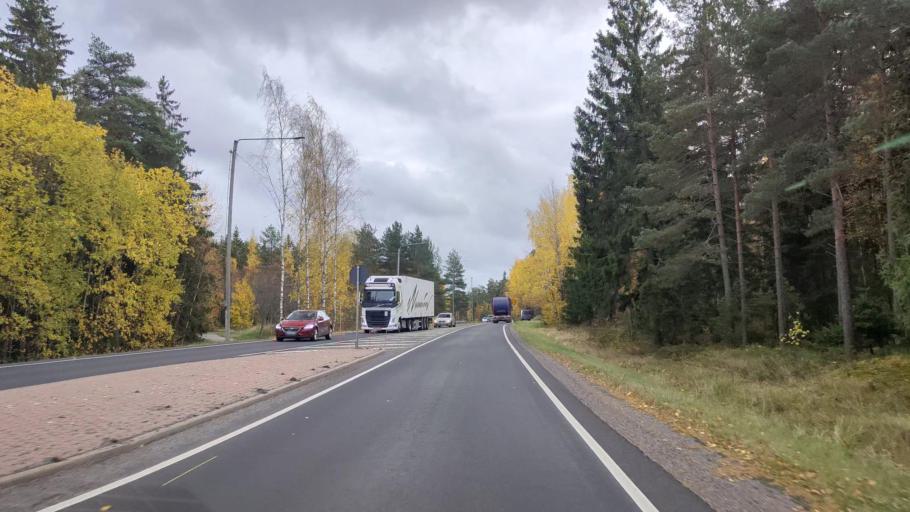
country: FI
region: Varsinais-Suomi
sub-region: Turku
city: Kaarina
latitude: 60.4580
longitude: 22.3655
